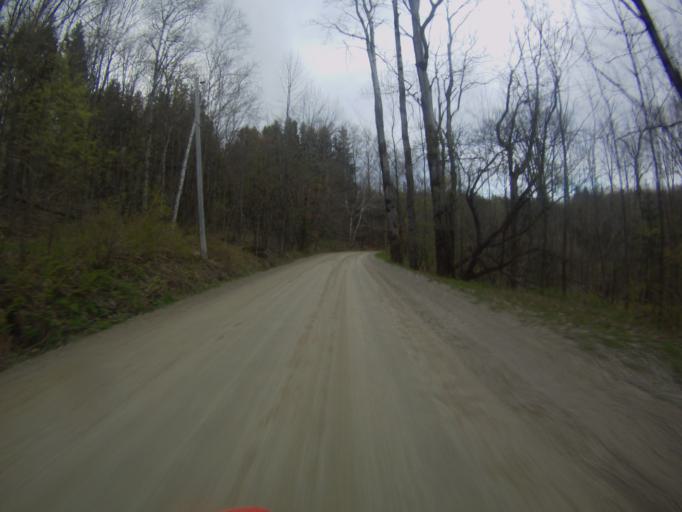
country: US
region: Vermont
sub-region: Addison County
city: Bristol
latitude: 44.0579
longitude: -73.0181
